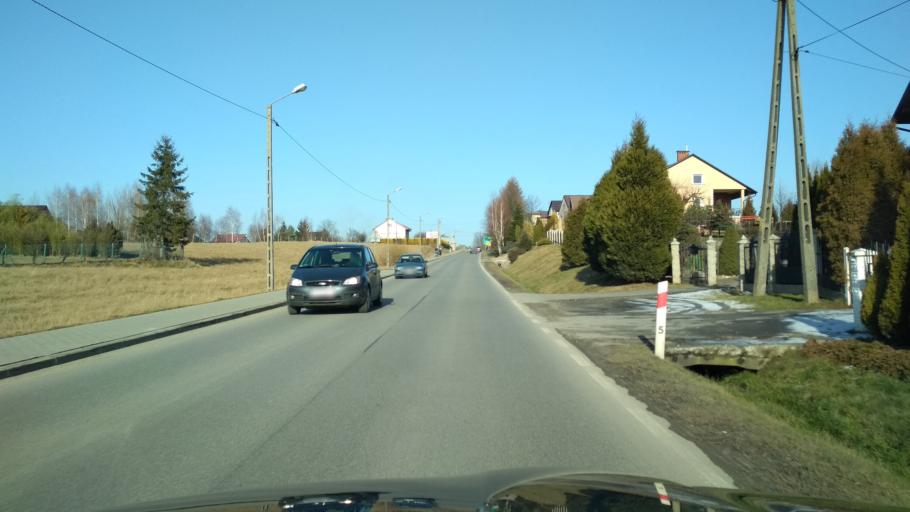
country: PL
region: Subcarpathian Voivodeship
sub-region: Powiat ropczycko-sedziszowski
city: Sedziszow Malopolski
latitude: 50.0787
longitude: 21.7209
